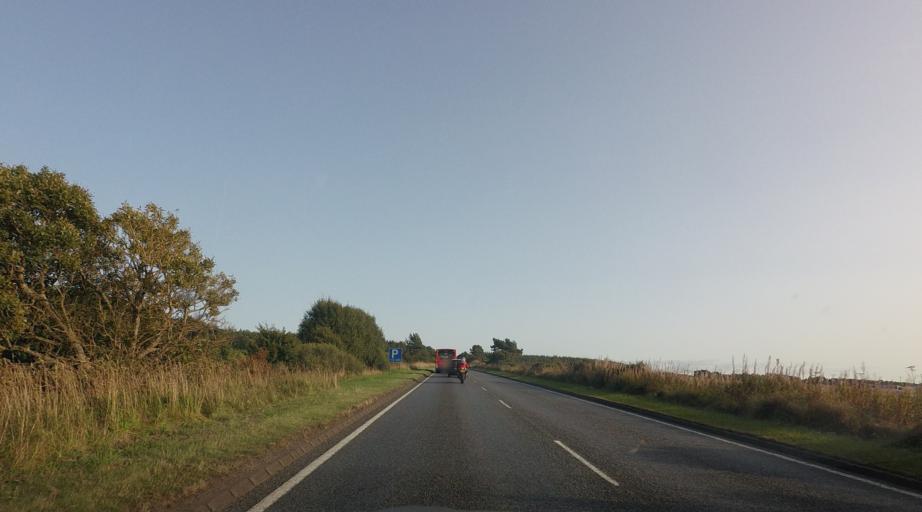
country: GB
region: Scotland
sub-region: Highland
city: Dingwall
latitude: 57.5717
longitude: -4.3512
